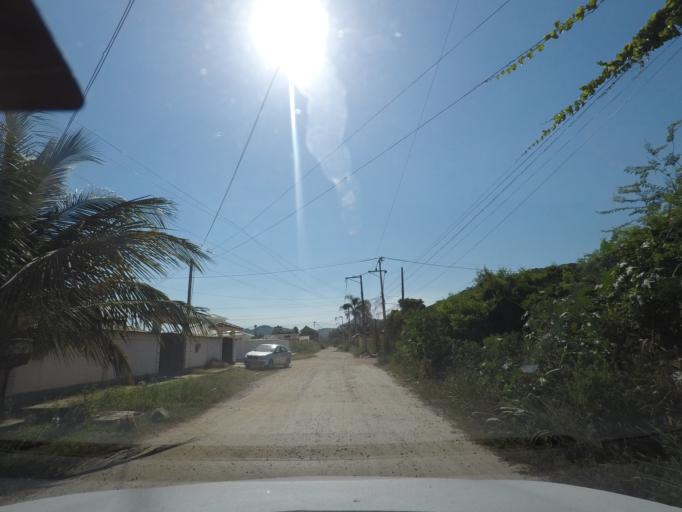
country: BR
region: Rio de Janeiro
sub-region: Niteroi
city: Niteroi
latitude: -22.9596
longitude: -42.9708
